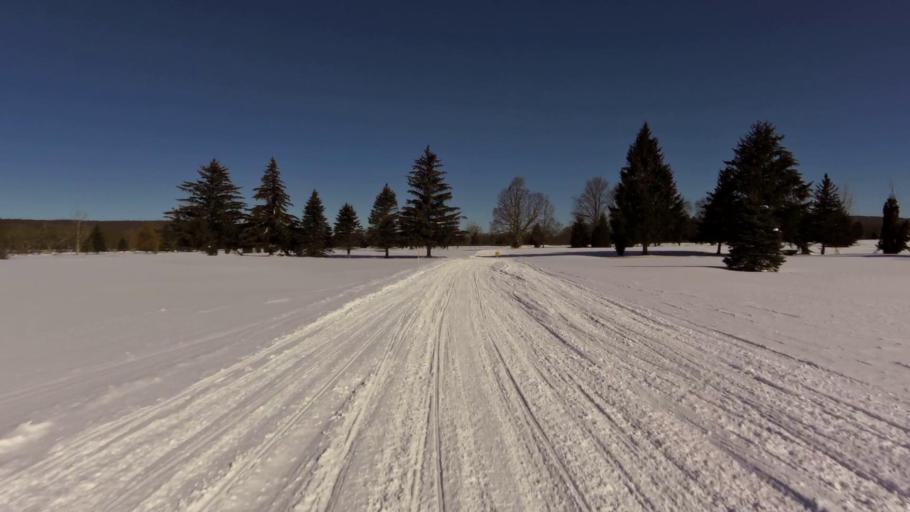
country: US
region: New York
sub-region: Cattaraugus County
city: Franklinville
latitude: 42.3567
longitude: -78.4556
